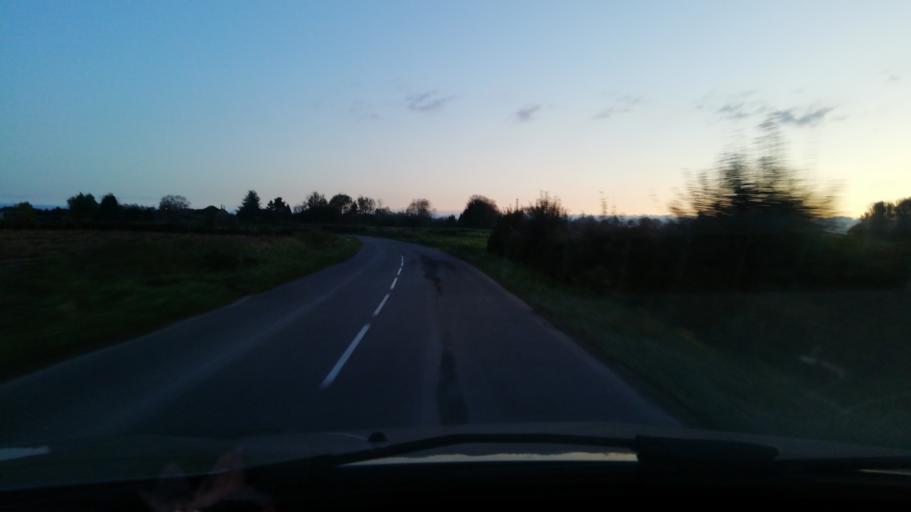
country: FR
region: Nord-Pas-de-Calais
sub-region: Departement du Nord
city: Marpent
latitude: 50.2700
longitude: 4.0865
